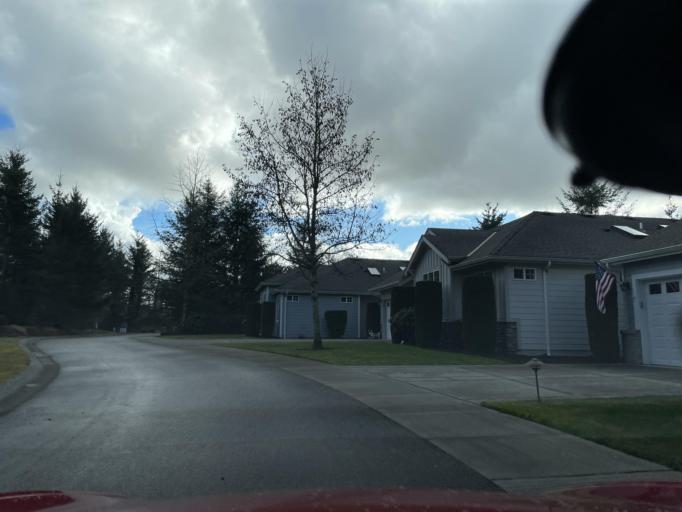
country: US
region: Washington
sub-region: Whatcom County
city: Lynden
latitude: 48.9408
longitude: -122.4749
